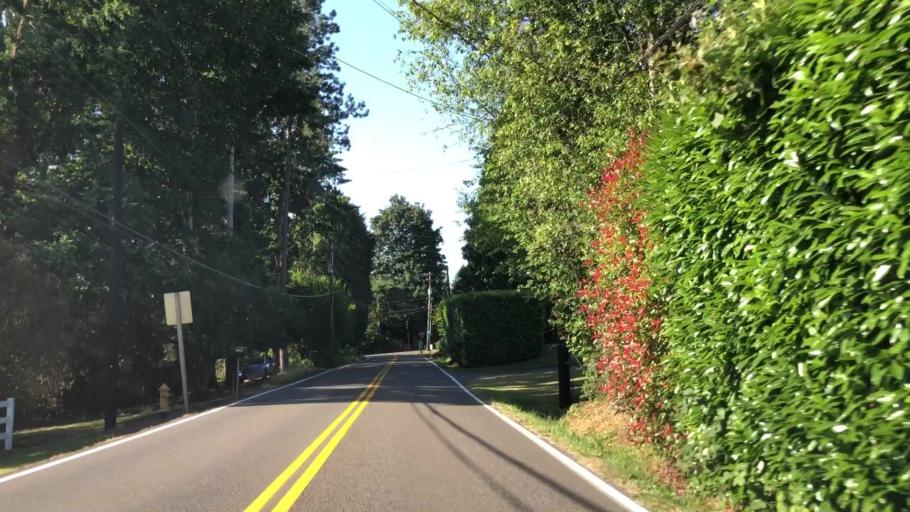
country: US
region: Washington
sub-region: King County
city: Woodinville
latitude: 47.7774
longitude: -122.1694
